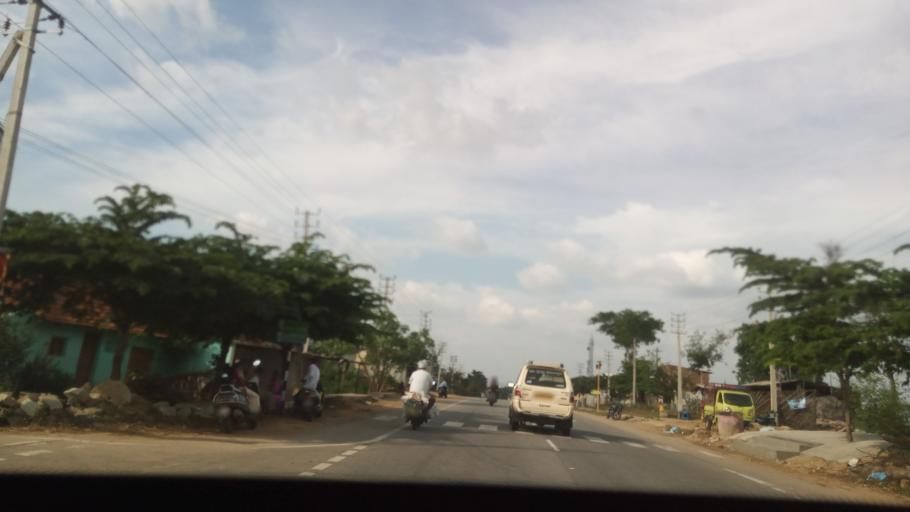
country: IN
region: Karnataka
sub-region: Mandya
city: Maddur
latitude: 12.6819
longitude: 77.0588
